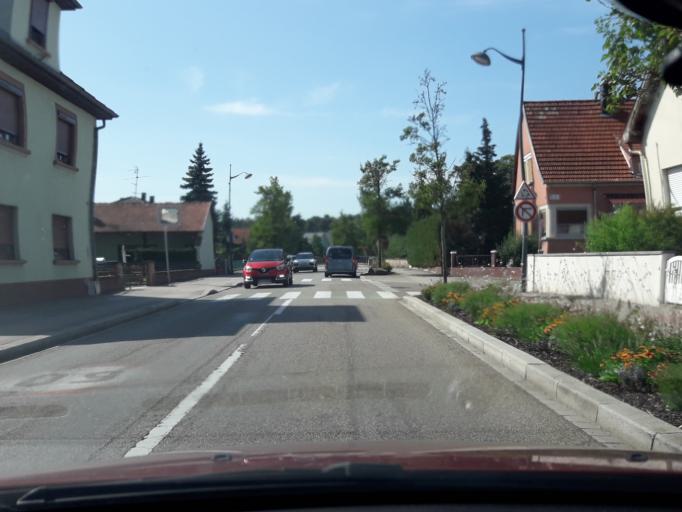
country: FR
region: Alsace
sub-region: Departement du Bas-Rhin
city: Schweighouse-sur-Moder
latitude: 48.8226
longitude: 7.7291
